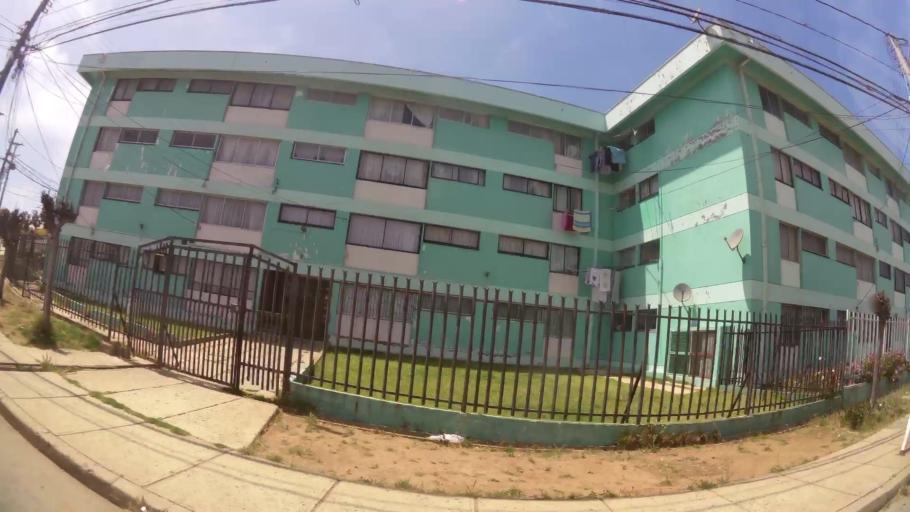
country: CL
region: Valparaiso
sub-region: Provincia de Valparaiso
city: Valparaiso
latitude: -33.0288
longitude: -71.6513
